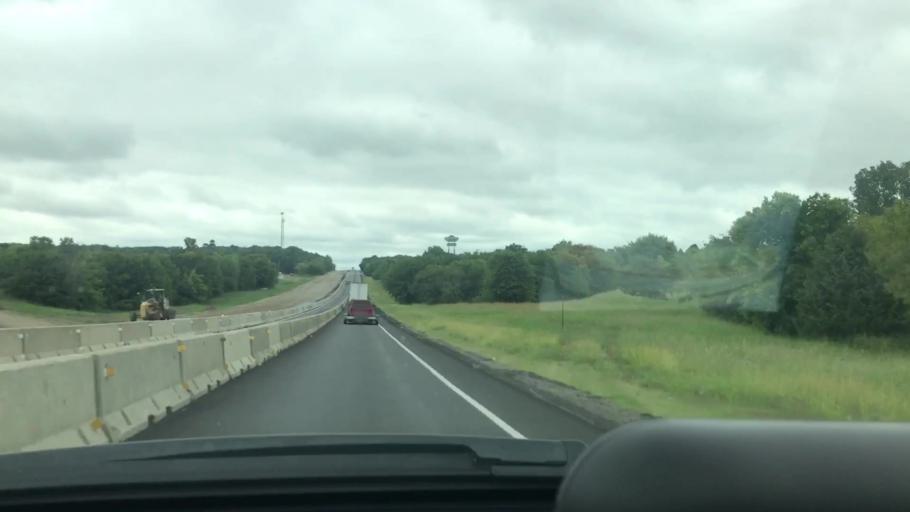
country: US
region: Oklahoma
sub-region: McIntosh County
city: Eufaula
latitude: 35.2783
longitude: -95.5931
